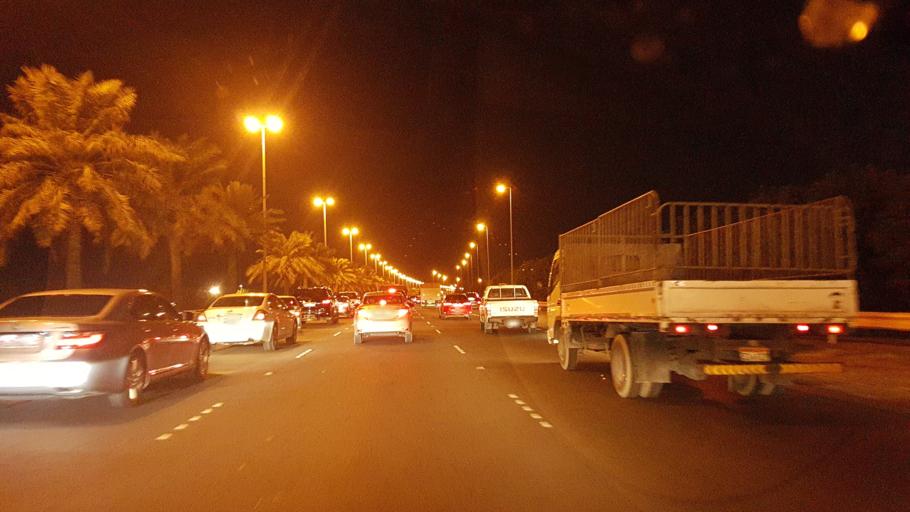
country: BH
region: Central Governorate
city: Madinat Hamad
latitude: 26.1595
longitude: 50.5052
